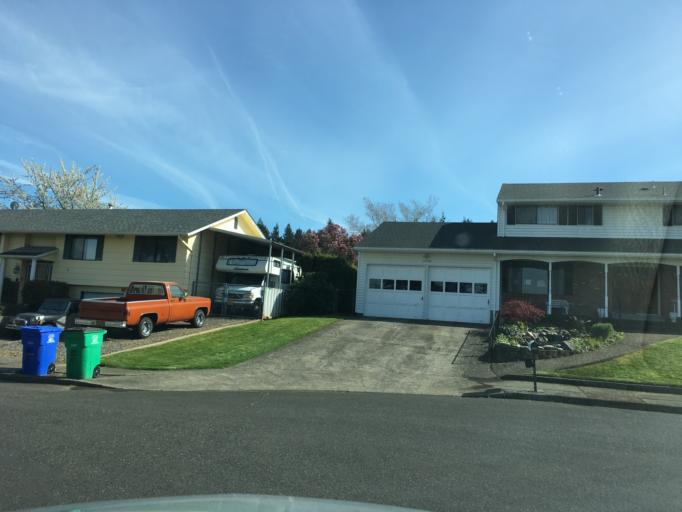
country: US
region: Oregon
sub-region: Multnomah County
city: Lents
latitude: 45.5426
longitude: -122.5313
